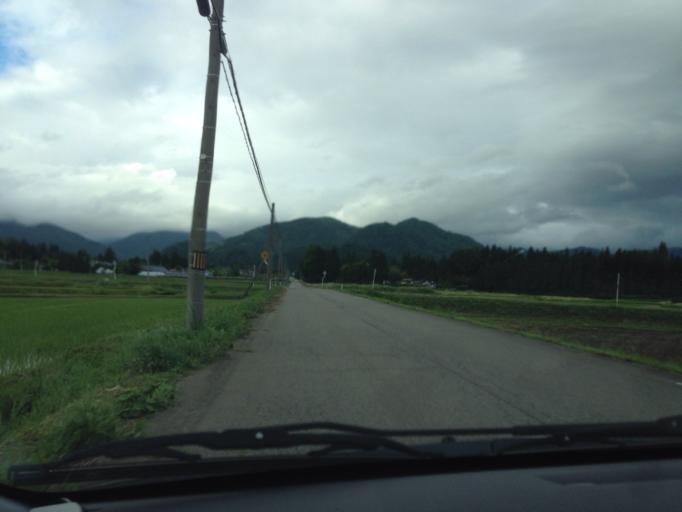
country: JP
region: Fukushima
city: Kitakata
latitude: 37.7151
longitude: 139.8594
